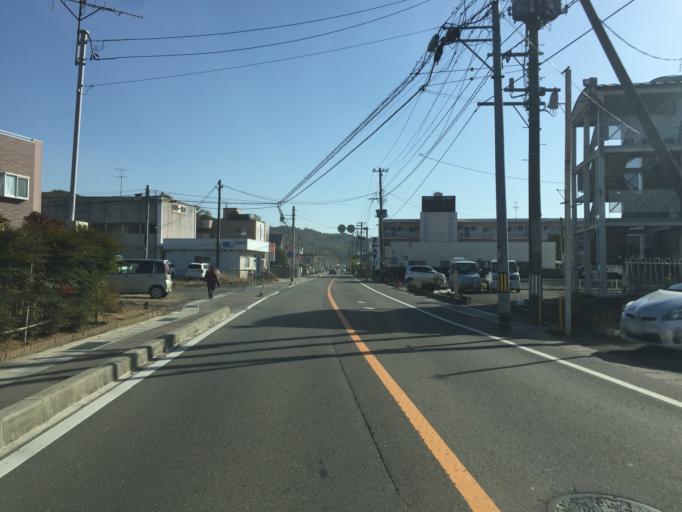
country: JP
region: Fukushima
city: Fukushima-shi
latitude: 37.7374
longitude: 140.4722
